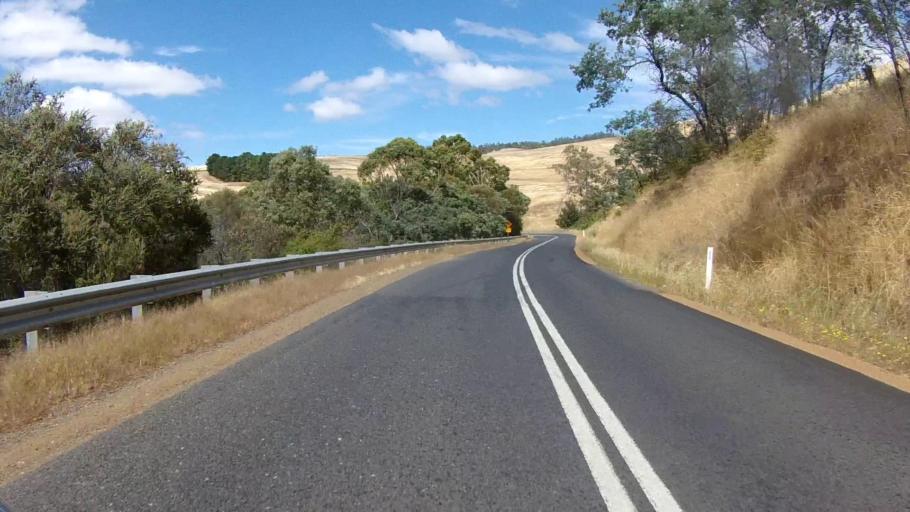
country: AU
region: Tasmania
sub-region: Brighton
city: Bridgewater
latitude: -42.5683
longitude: 147.3887
